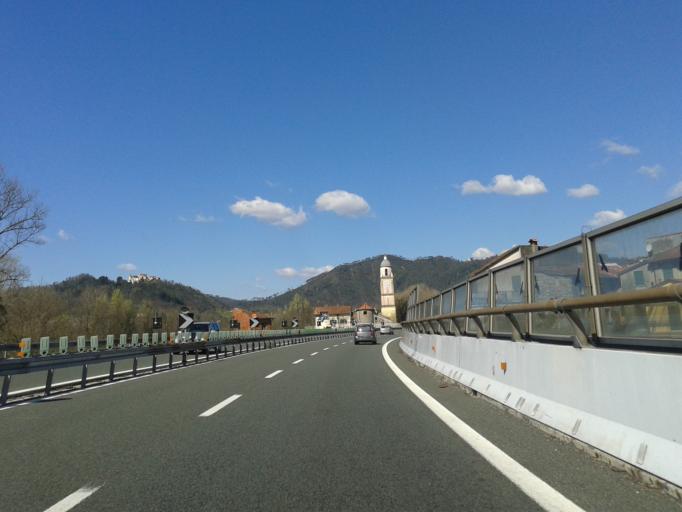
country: IT
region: Liguria
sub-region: Provincia di La Spezia
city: Beverino
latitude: 44.1984
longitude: 9.8128
